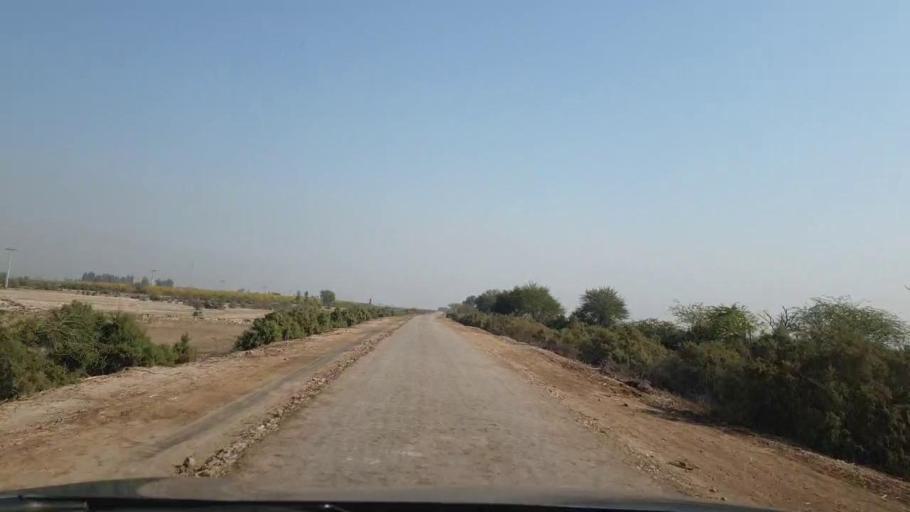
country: PK
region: Sindh
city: Berani
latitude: 25.6348
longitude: 68.8657
